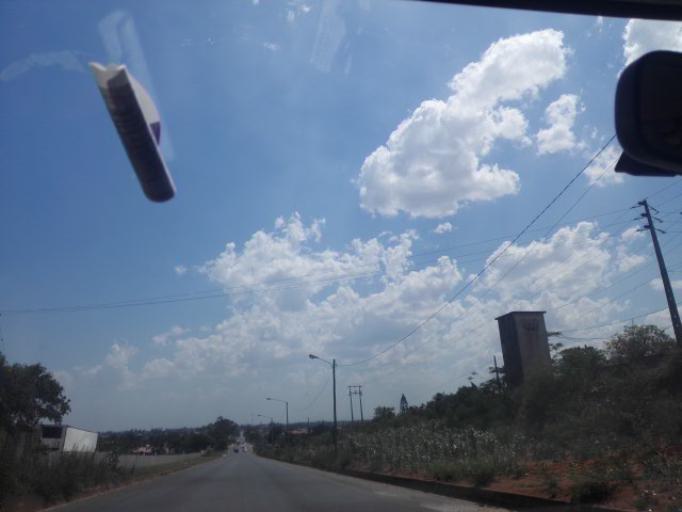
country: MZ
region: Maputo
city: Matola
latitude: -25.9640
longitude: 32.4469
